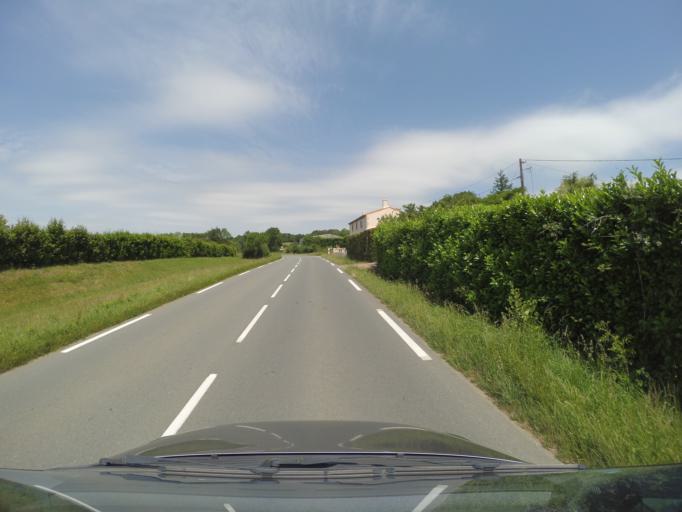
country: FR
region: Pays de la Loire
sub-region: Departement de la Vendee
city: Saint-Michel-Mont-Mercure
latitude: 46.8376
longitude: -0.9070
